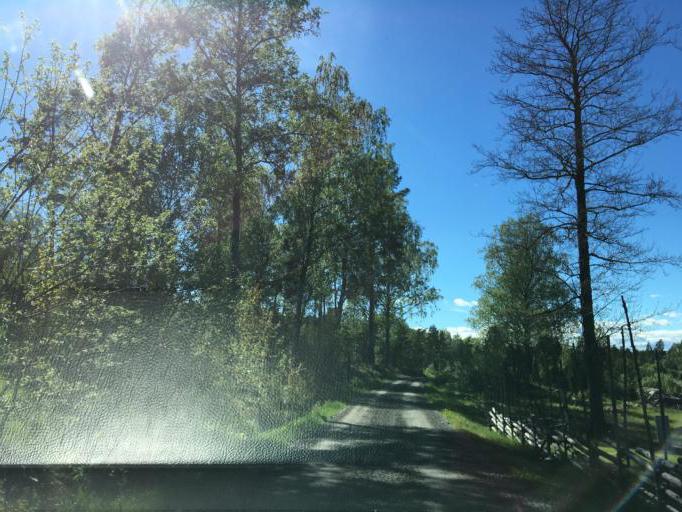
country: SE
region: Soedermanland
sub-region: Eskilstuna Kommun
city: Kvicksund
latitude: 59.3487
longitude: 16.3224
